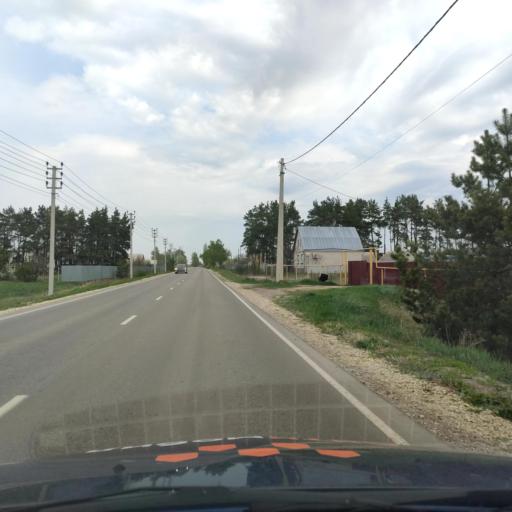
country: RU
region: Voronezj
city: Podgornoye
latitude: 51.8748
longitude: 39.1732
